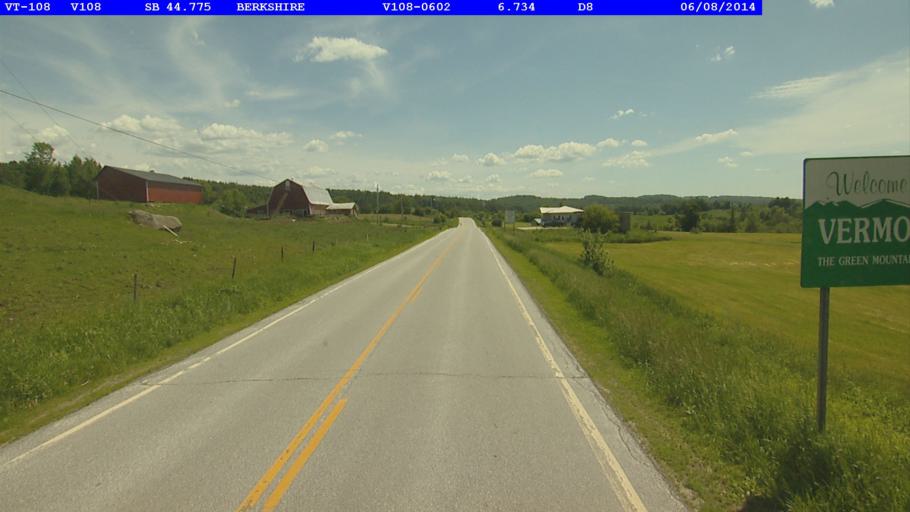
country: US
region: Vermont
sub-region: Franklin County
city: Enosburg Falls
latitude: 45.0140
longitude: -72.8254
